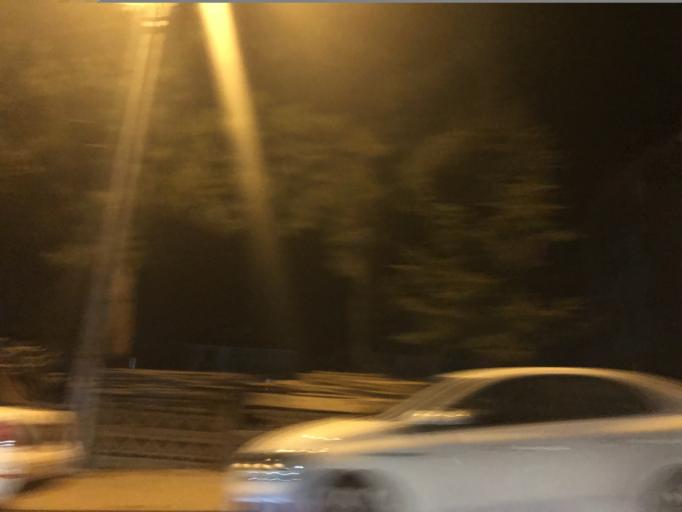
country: TR
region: Karabuk
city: Safranbolu
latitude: 41.2561
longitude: 32.6816
